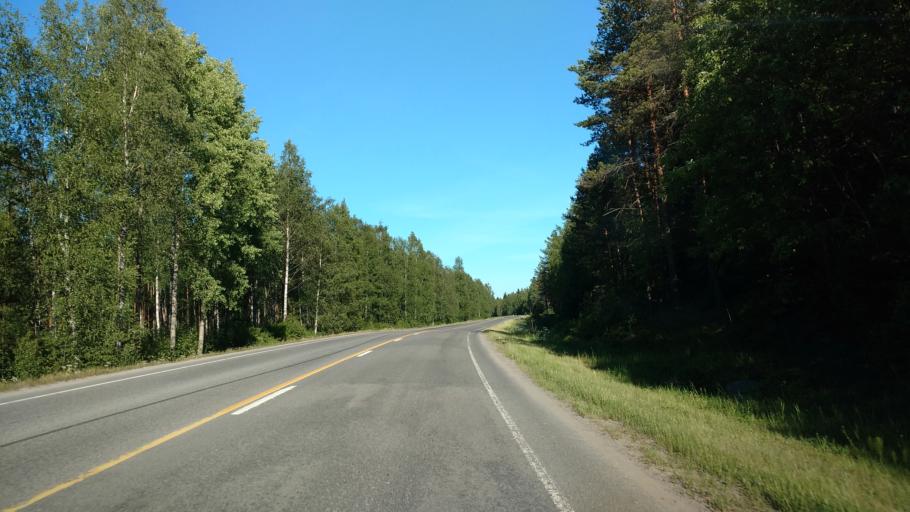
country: FI
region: Varsinais-Suomi
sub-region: Salo
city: Salo
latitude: 60.3823
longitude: 23.2002
